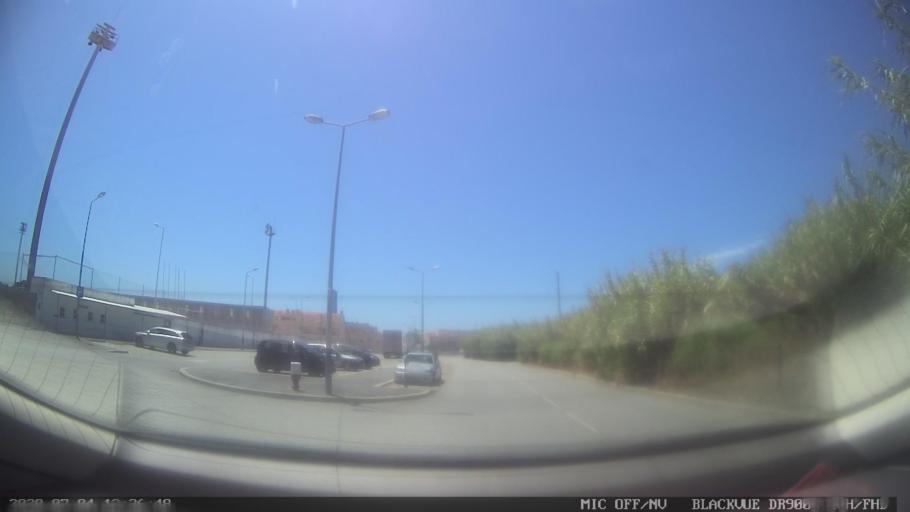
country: PT
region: Porto
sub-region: Matosinhos
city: Lavra
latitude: 41.2546
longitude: -8.7191
